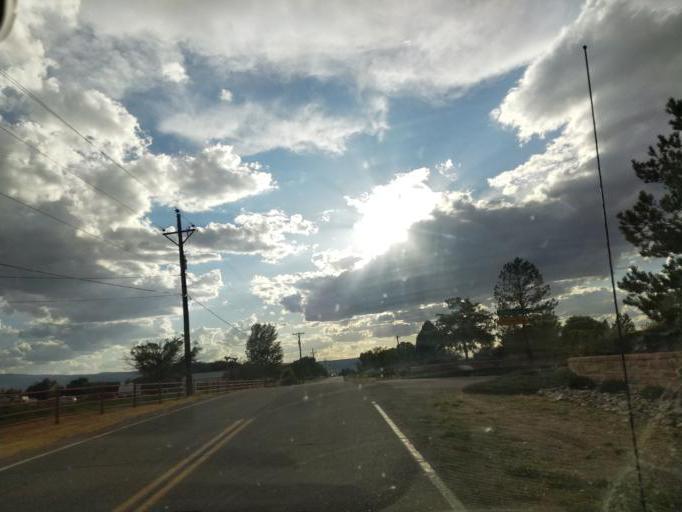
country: US
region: Colorado
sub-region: Mesa County
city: Clifton
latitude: 39.0558
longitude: -108.4441
